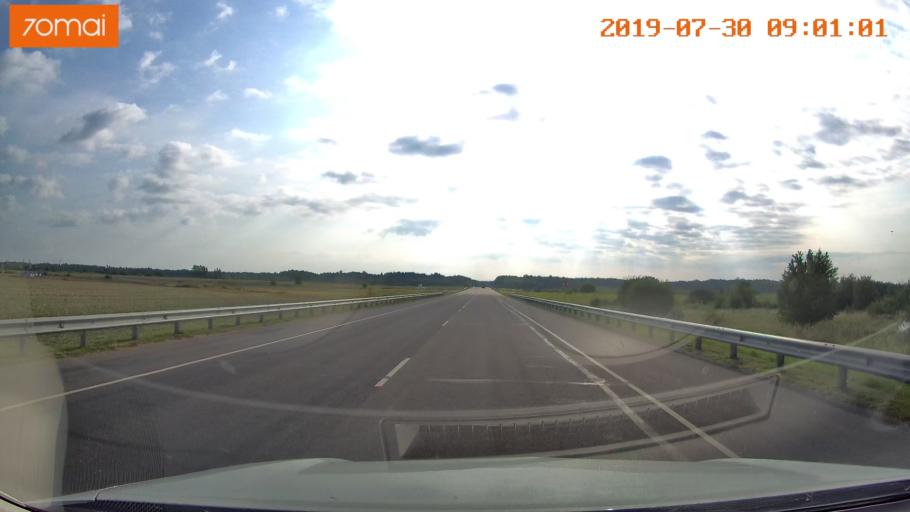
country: RU
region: Kaliningrad
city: Gusev
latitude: 54.6156
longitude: 22.1973
